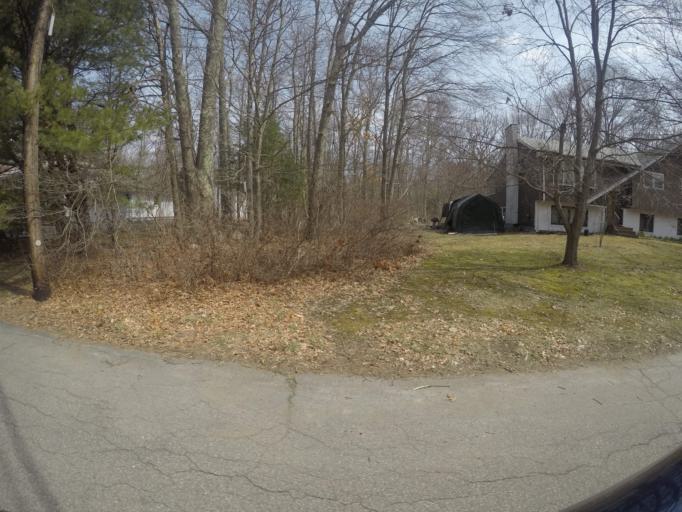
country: US
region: Massachusetts
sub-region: Bristol County
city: Easton
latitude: 42.0498
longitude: -71.1062
